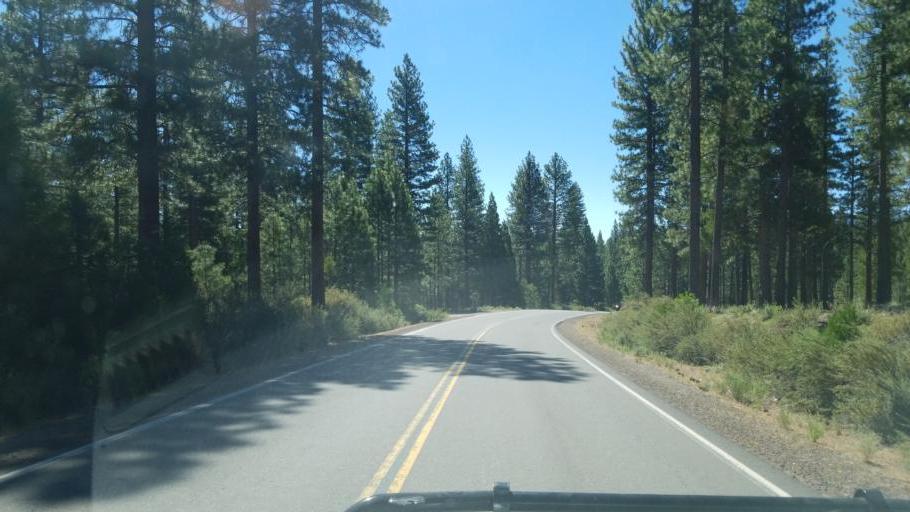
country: US
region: California
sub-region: Lassen County
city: Susanville
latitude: 40.4325
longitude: -120.7320
